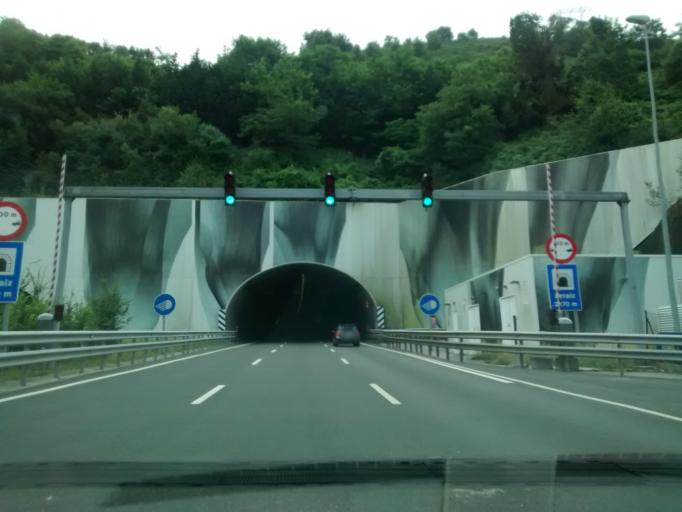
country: ES
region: Basque Country
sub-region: Bizkaia
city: Alonsotegi
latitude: 43.2505
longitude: -2.9737
